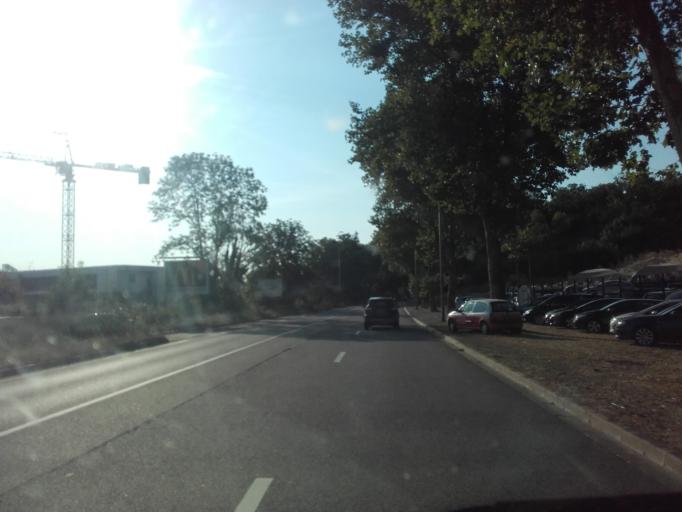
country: FR
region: Bourgogne
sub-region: Departement de l'Yonne
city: Augy
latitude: 47.7891
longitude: 3.5943
